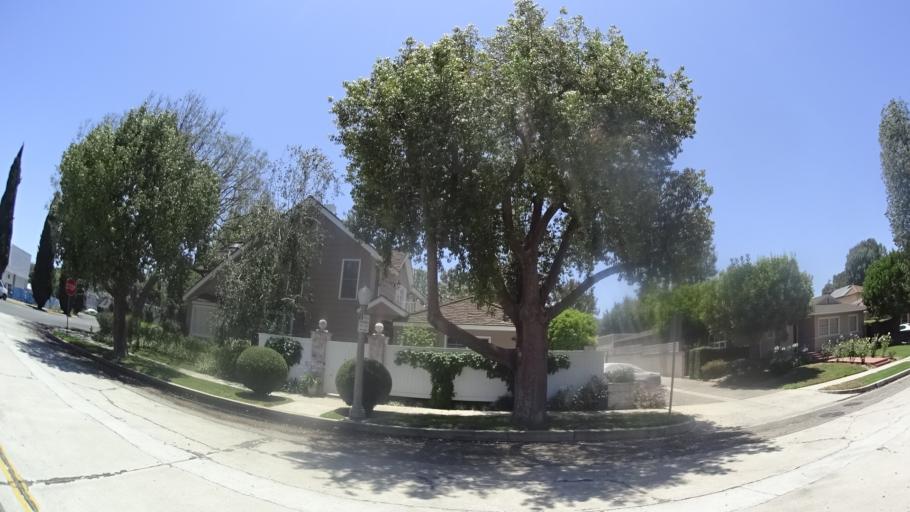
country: US
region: California
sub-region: Los Angeles County
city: Sherman Oaks
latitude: 34.1515
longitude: -118.4705
